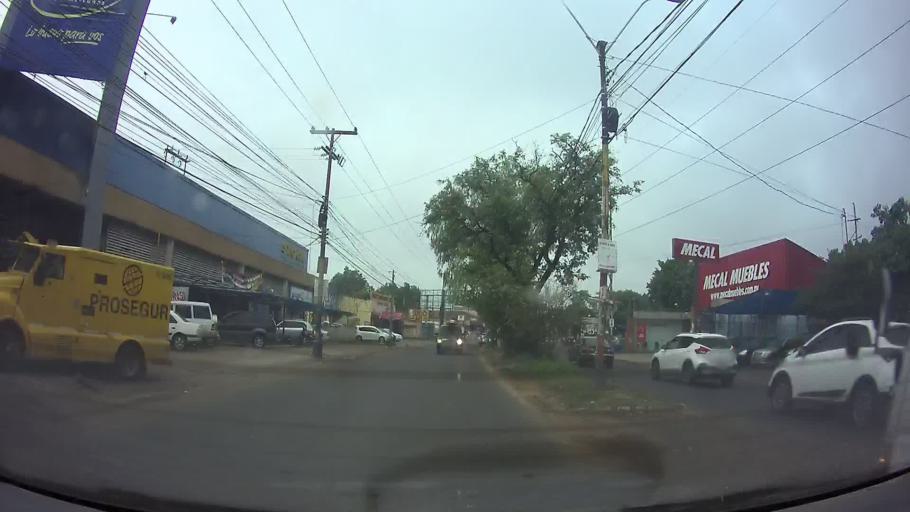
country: PY
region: Central
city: Fernando de la Mora
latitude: -25.3060
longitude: -57.5344
